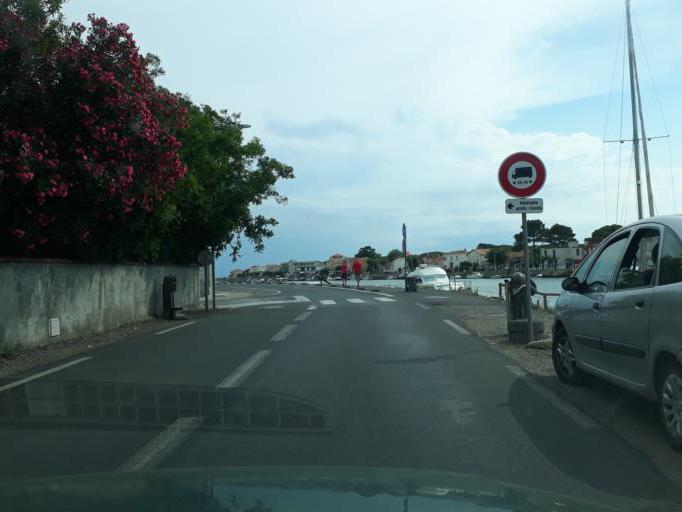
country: FR
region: Languedoc-Roussillon
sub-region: Departement de l'Herault
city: Vias
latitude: 43.2895
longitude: 3.4453
